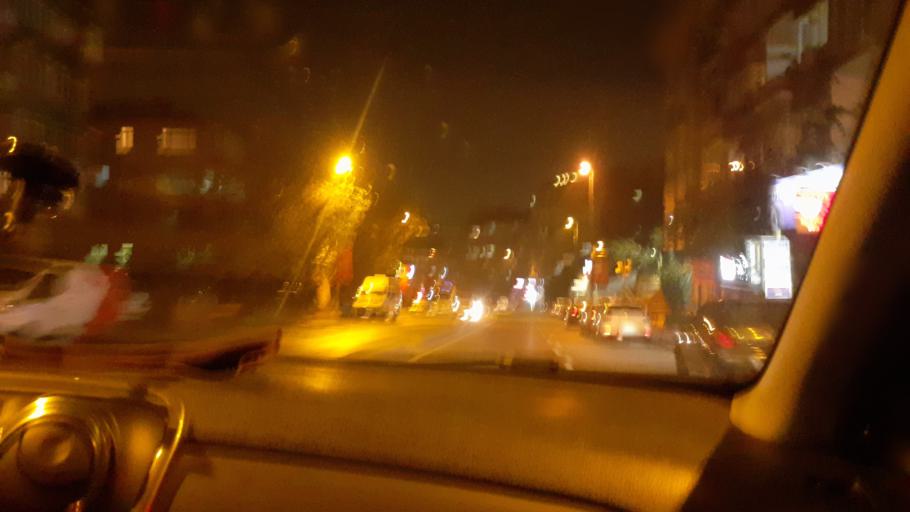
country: TR
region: Istanbul
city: UEskuedar
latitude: 41.0280
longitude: 29.0296
